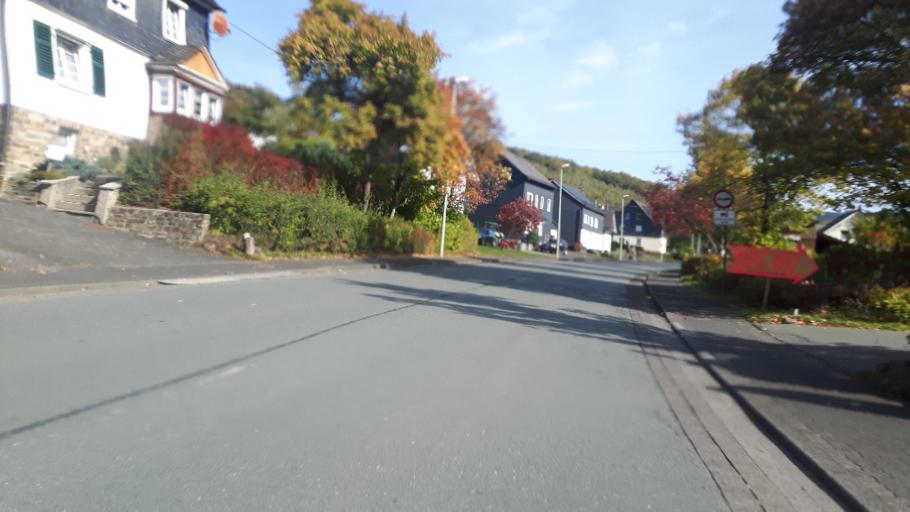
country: DE
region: North Rhine-Westphalia
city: Netphen
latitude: 50.8956
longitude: 8.1917
